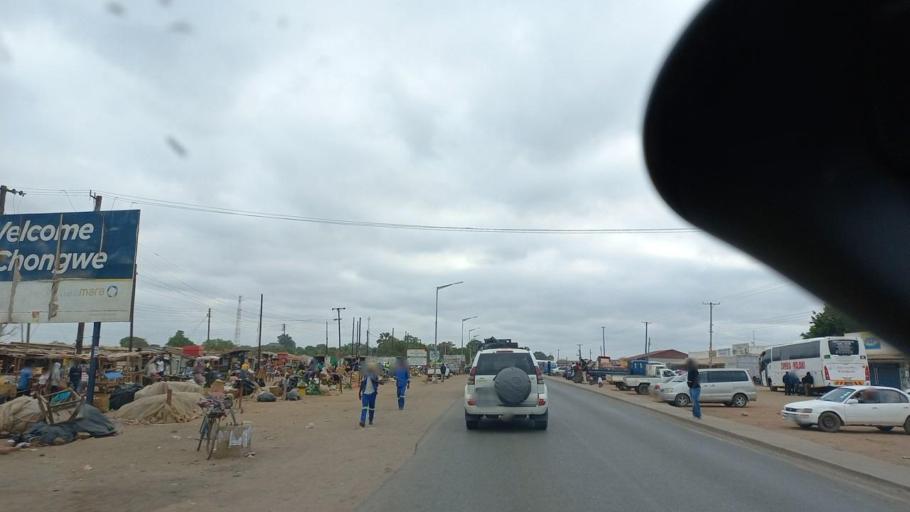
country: ZM
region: Lusaka
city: Chongwe
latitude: -15.3316
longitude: 28.6747
